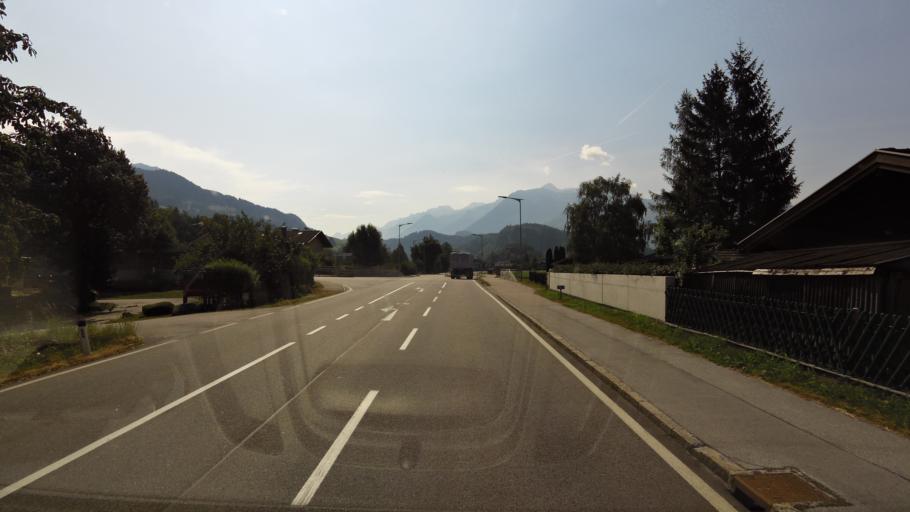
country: AT
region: Salzburg
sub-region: Politischer Bezirk Hallein
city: Golling an der Salzach
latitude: 47.6148
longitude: 13.1644
